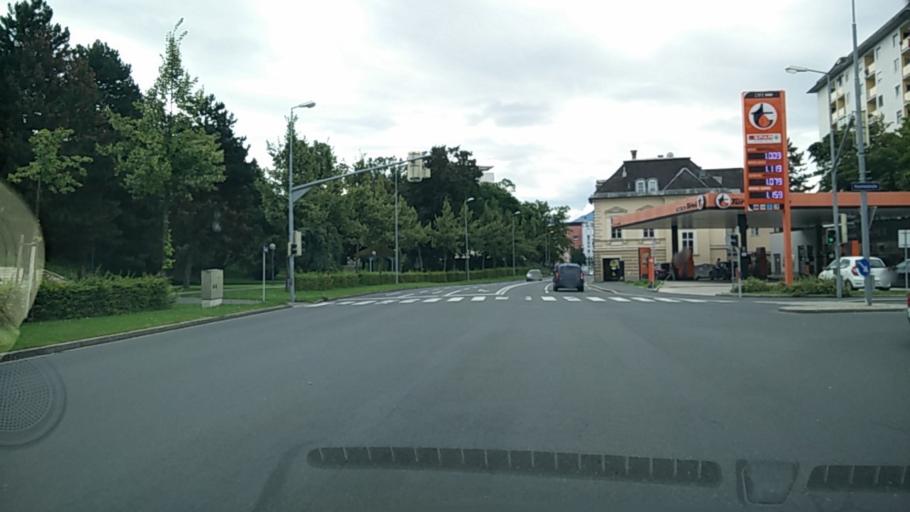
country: AT
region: Carinthia
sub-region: Klagenfurt am Woerthersee
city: Klagenfurt am Woerthersee
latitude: 46.6261
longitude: 14.3025
